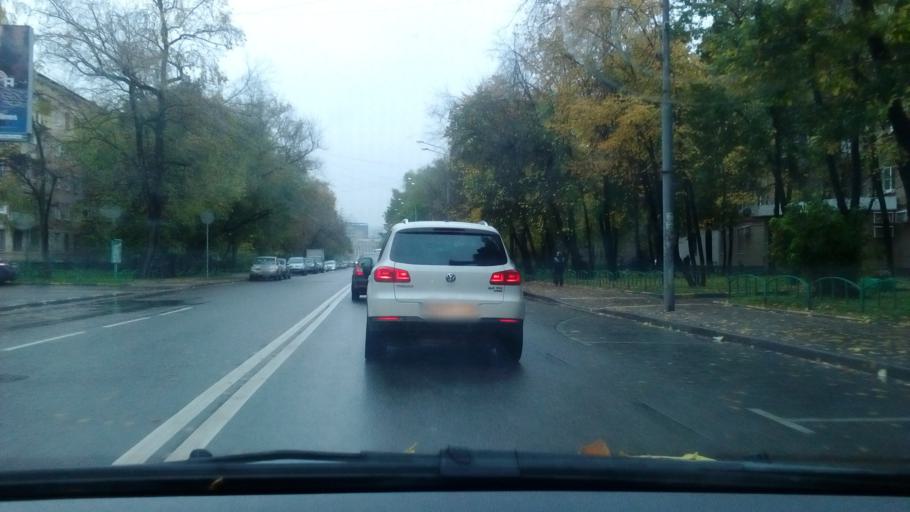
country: RU
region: Moscow
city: Mar'ina Roshcha
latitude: 55.7973
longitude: 37.5762
